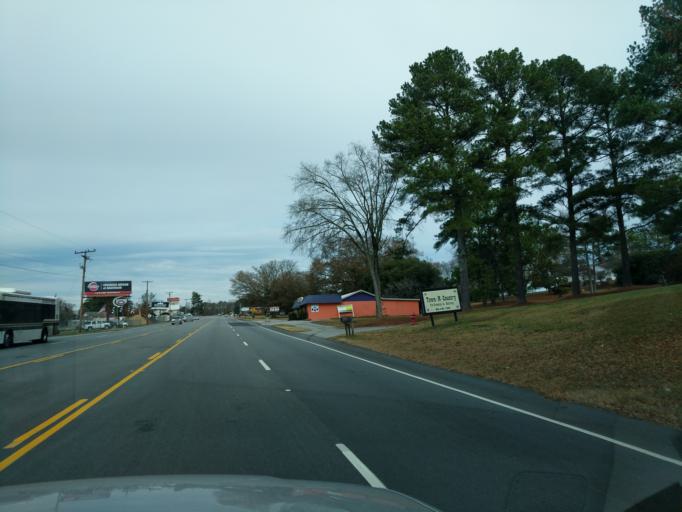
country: US
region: South Carolina
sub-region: Anderson County
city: Pendleton
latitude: 34.6062
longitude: -82.7650
